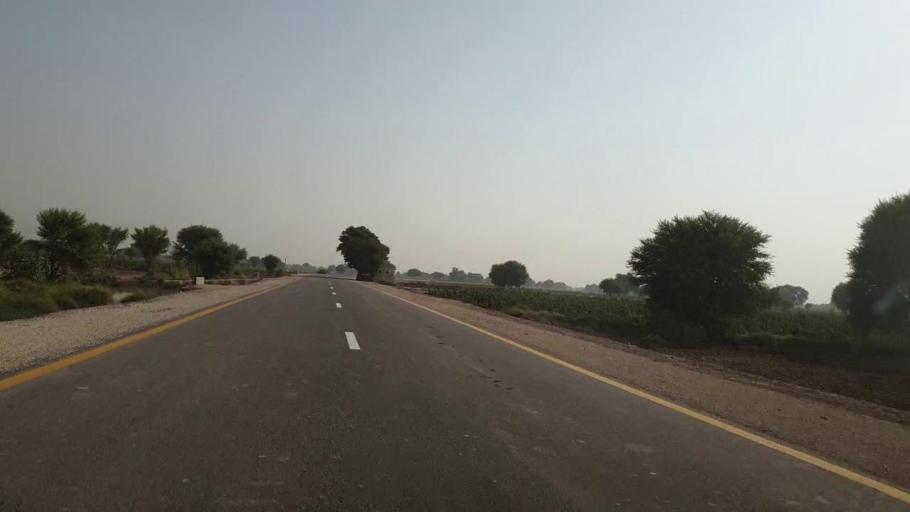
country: PK
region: Sindh
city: Bhan
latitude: 26.5283
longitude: 67.7893
